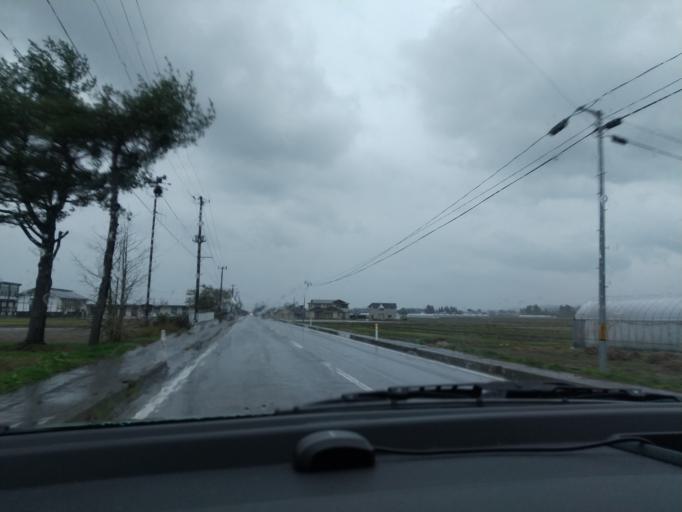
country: JP
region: Akita
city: Omagari
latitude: 39.3934
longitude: 140.5335
